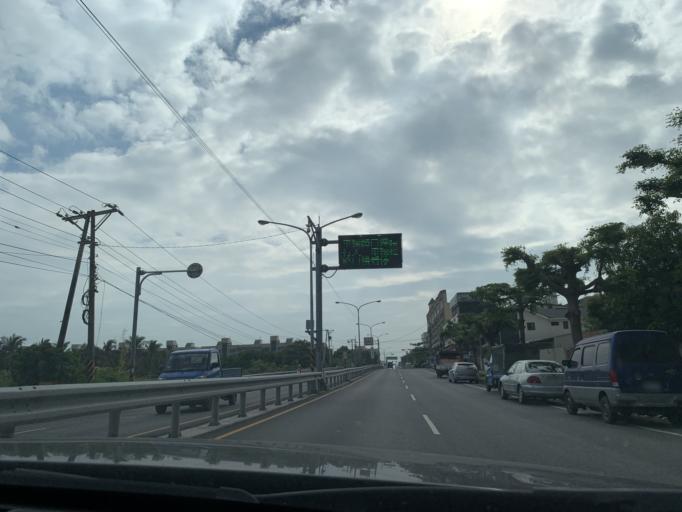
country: TW
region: Taiwan
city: Fengshan
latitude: 22.4655
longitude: 120.4630
